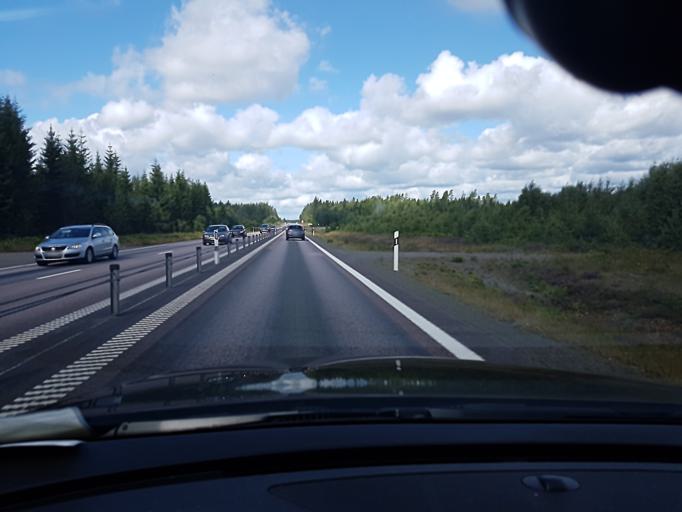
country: SE
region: Kalmar
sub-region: Emmaboda Kommun
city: Emmaboda
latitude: 56.7306
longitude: 15.5481
